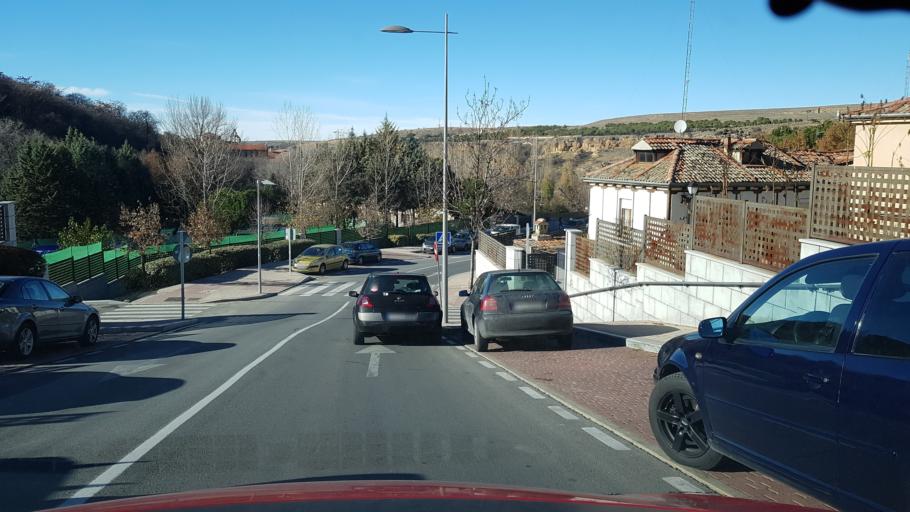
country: ES
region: Castille and Leon
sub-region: Provincia de Segovia
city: Segovia
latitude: 40.9515
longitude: -4.1137
